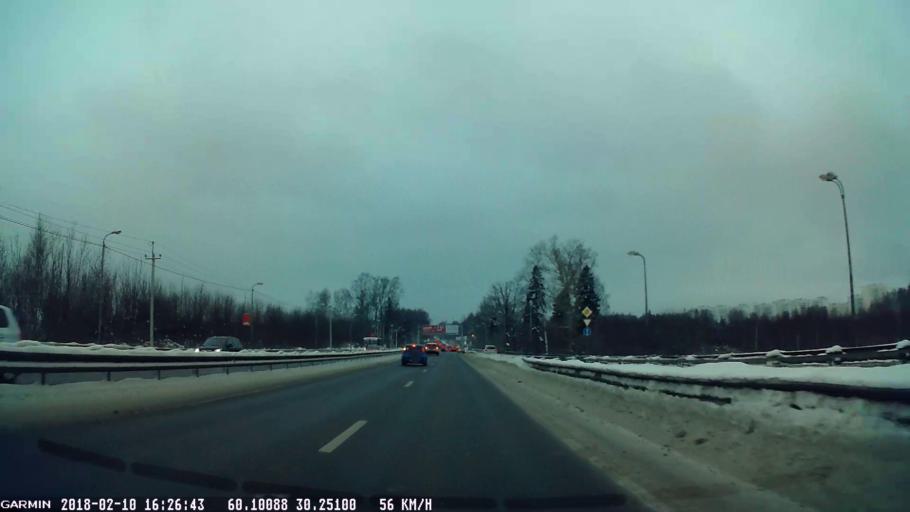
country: RU
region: St.-Petersburg
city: Pargolovo
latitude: 60.1012
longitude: 30.2508
